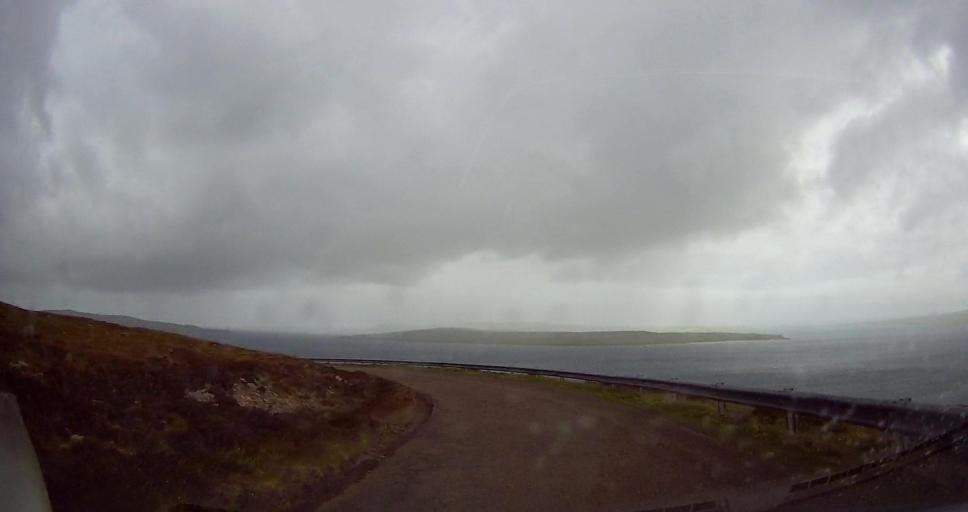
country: GB
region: Scotland
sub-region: Orkney Islands
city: Stromness
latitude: 58.8993
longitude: -3.2743
